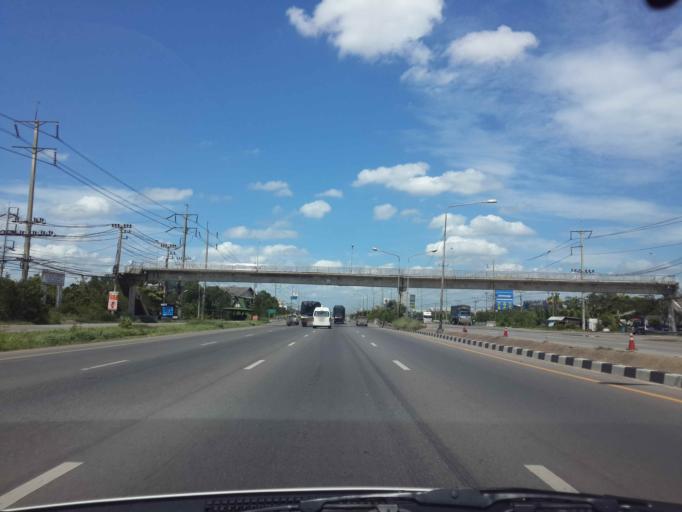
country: TH
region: Samut Sakhon
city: Samut Sakhon
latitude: 13.5307
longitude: 100.2025
